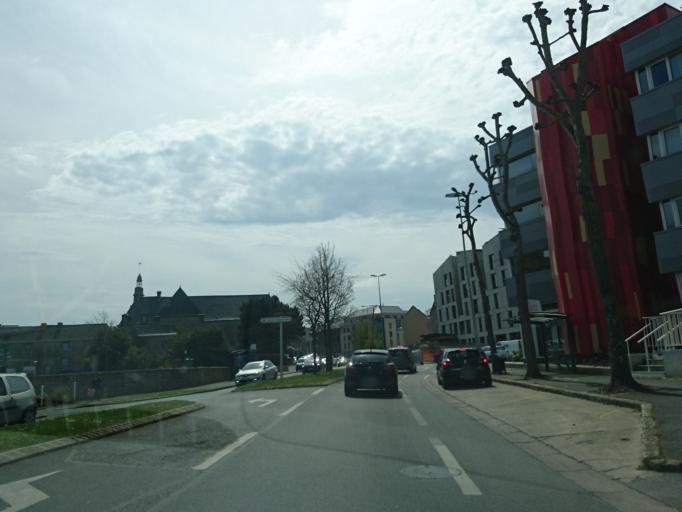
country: FR
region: Brittany
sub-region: Departement d'Ille-et-Vilaine
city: Saint-Malo
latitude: 48.6386
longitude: -2.0092
